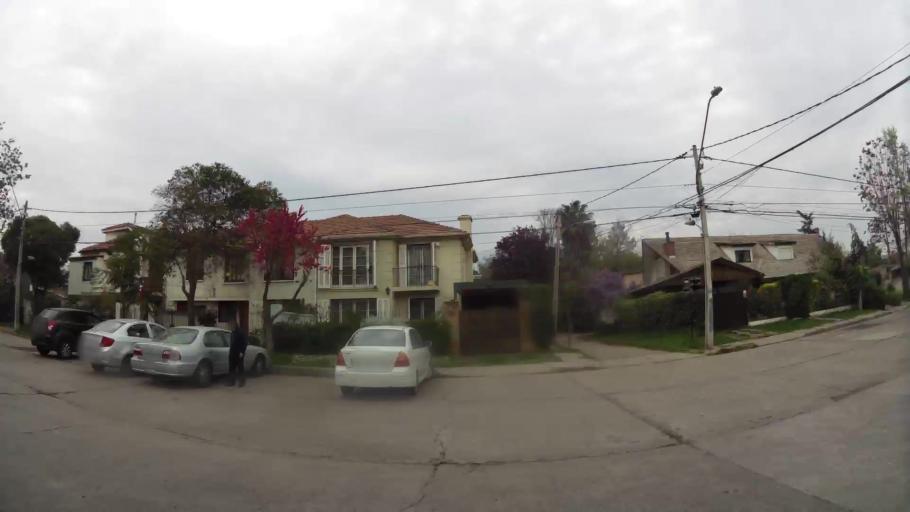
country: CL
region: Santiago Metropolitan
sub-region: Provincia de Santiago
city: Villa Presidente Frei, Nunoa, Santiago, Chile
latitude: -33.4631
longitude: -70.5897
